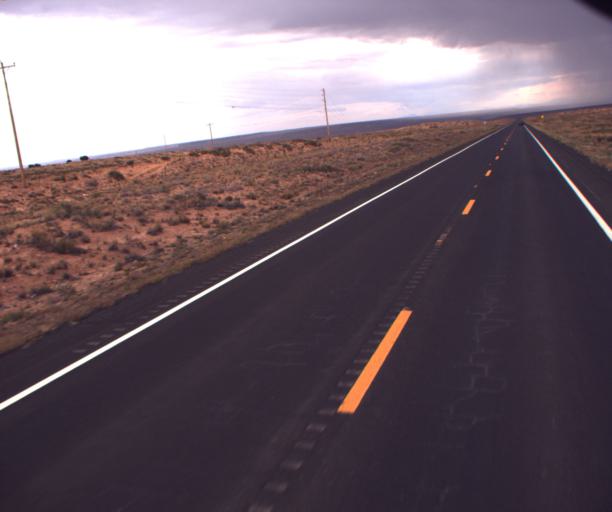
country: US
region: Arizona
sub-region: Coconino County
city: Tuba City
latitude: 36.2327
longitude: -111.0302
